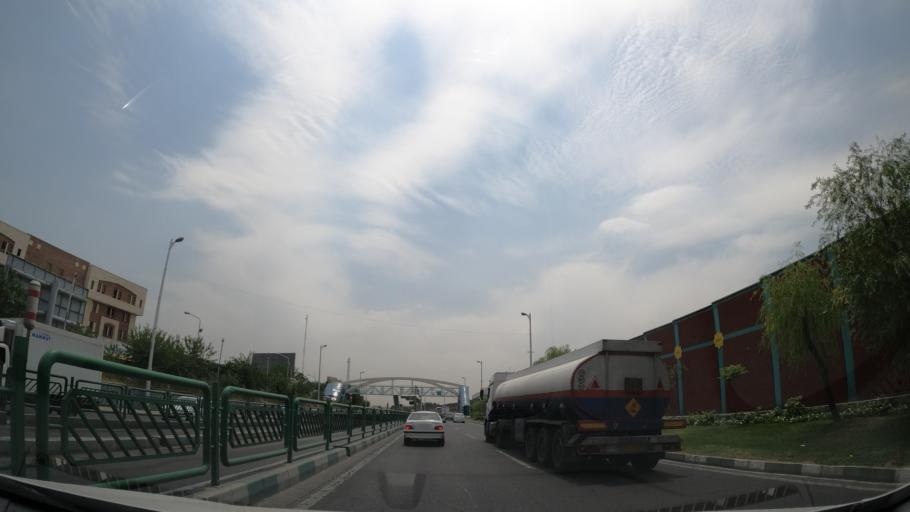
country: IR
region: Tehran
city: Tehran
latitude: 35.6899
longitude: 51.3406
